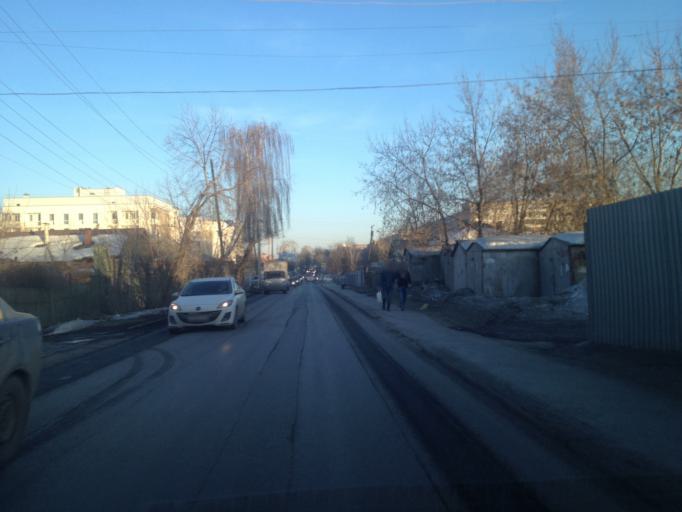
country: RU
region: Sverdlovsk
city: Sovkhoznyy
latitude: 56.8063
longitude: 60.5736
